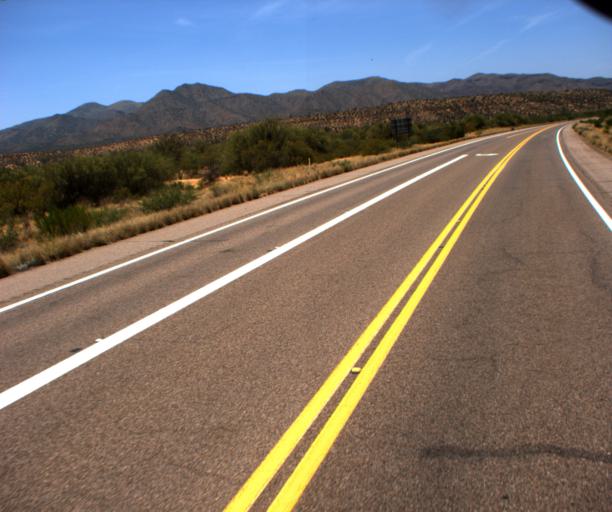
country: US
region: Arizona
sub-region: Gila County
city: Miami
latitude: 33.6181
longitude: -111.0527
